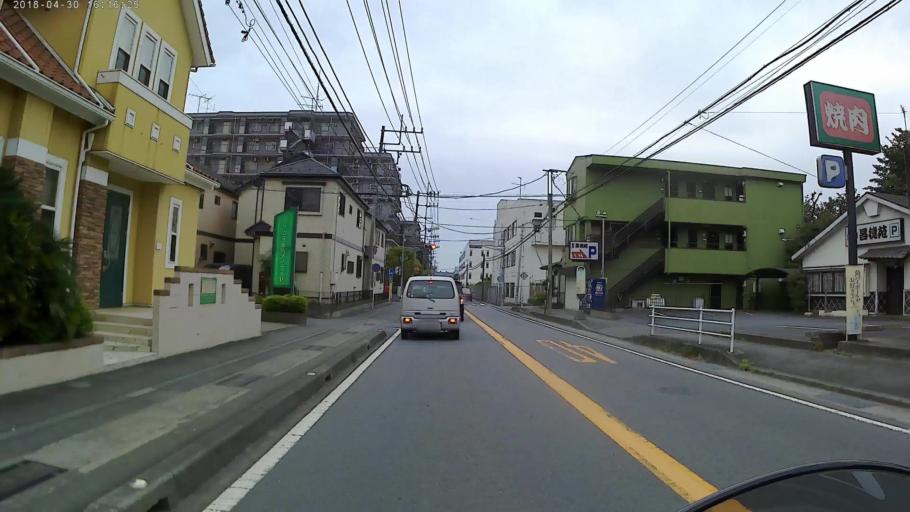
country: JP
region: Kanagawa
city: Minami-rinkan
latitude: 35.4831
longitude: 139.4317
